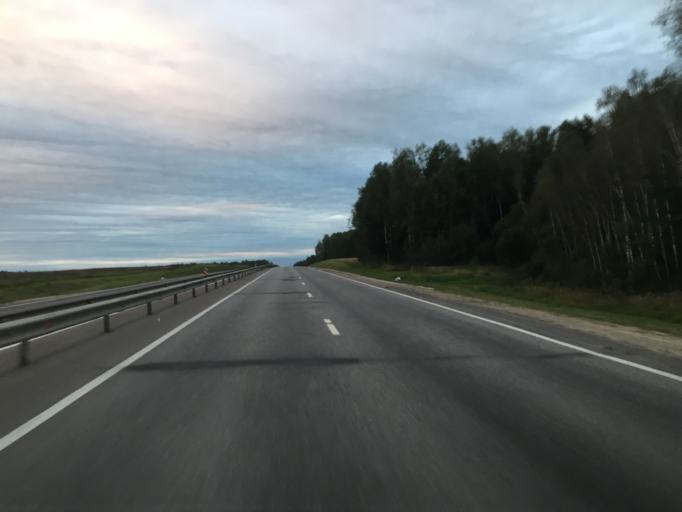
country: RU
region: Kaluga
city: Kaluga
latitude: 54.6488
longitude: 36.2927
